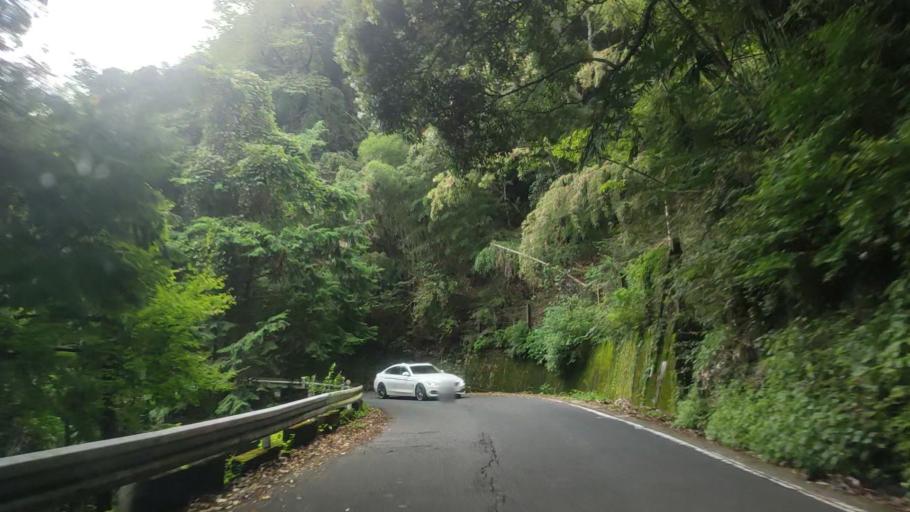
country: JP
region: Wakayama
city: Koya
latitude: 34.2423
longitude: 135.5470
